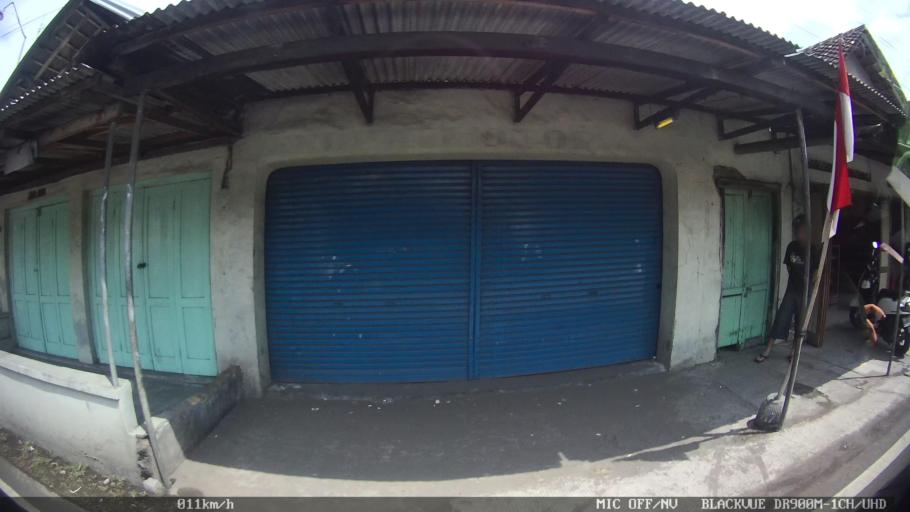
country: ID
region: Daerah Istimewa Yogyakarta
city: Depok
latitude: -7.8375
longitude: 110.4763
